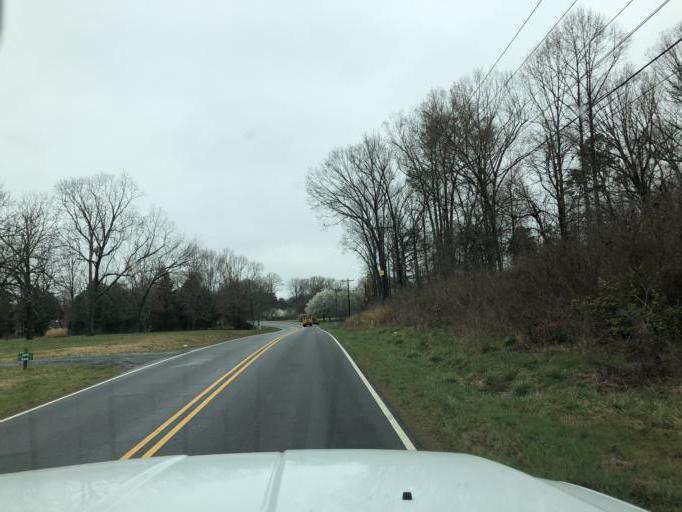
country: US
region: North Carolina
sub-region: Gaston County
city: Mount Holly
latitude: 35.3350
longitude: -80.9305
